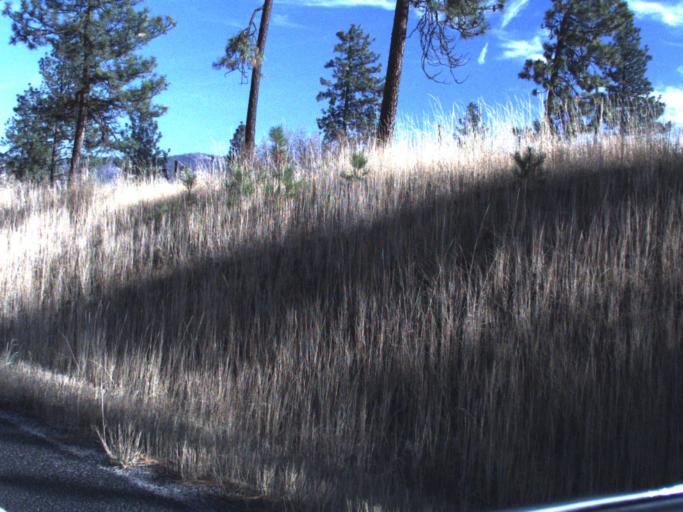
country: US
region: Washington
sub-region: Lincoln County
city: Davenport
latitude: 48.0079
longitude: -118.2606
